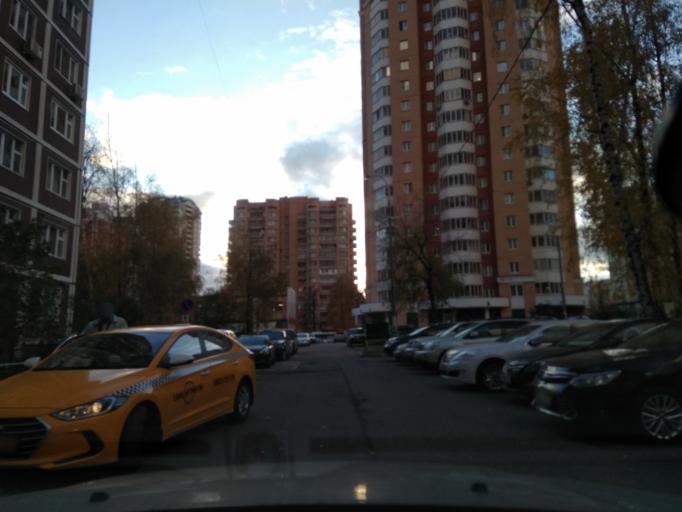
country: RU
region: Moskovskaya
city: Vostochnoe Degunino
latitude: 55.8684
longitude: 37.5592
